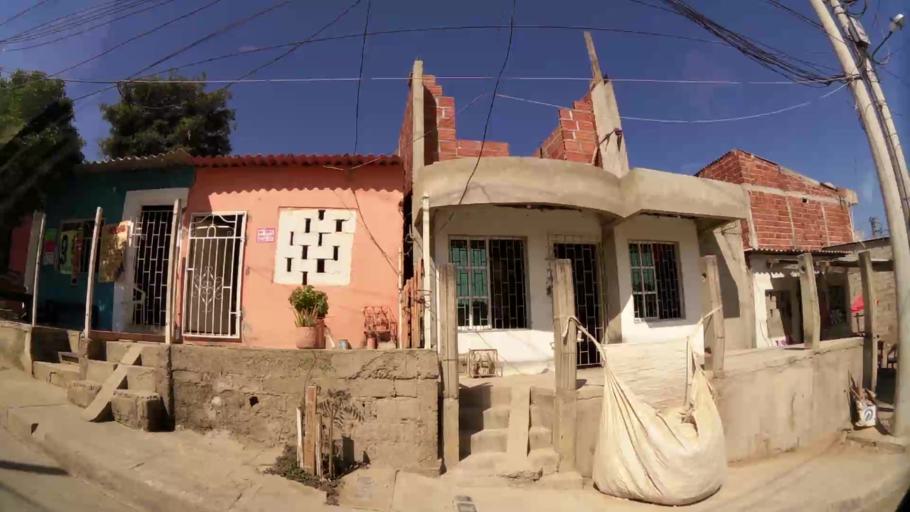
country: CO
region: Bolivar
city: Cartagena
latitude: 10.3696
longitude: -75.4970
